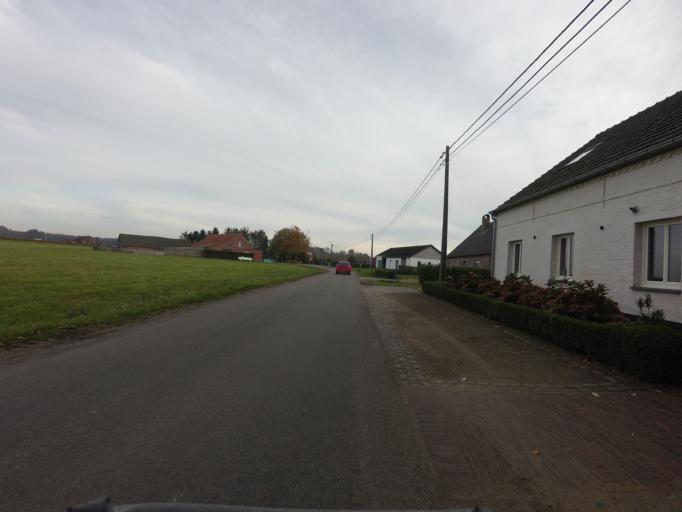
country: BE
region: Flanders
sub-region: Provincie Antwerpen
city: Hoogstraten
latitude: 51.4526
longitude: 4.7545
